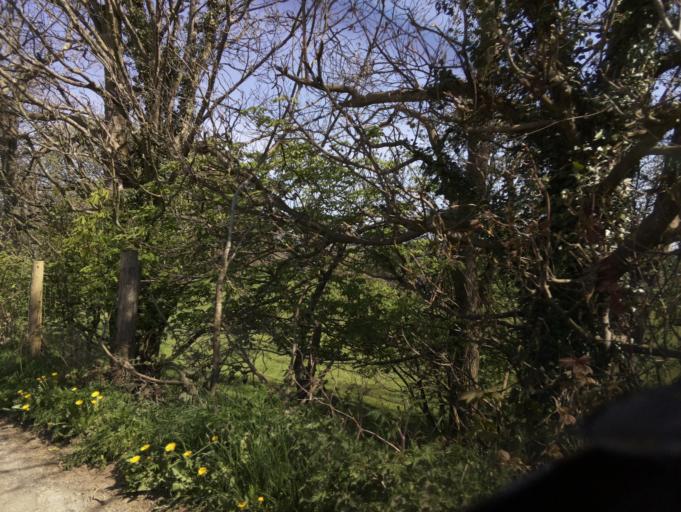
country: GB
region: Wales
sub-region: Monmouthshire
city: Chepstow
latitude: 51.6541
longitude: -2.7241
